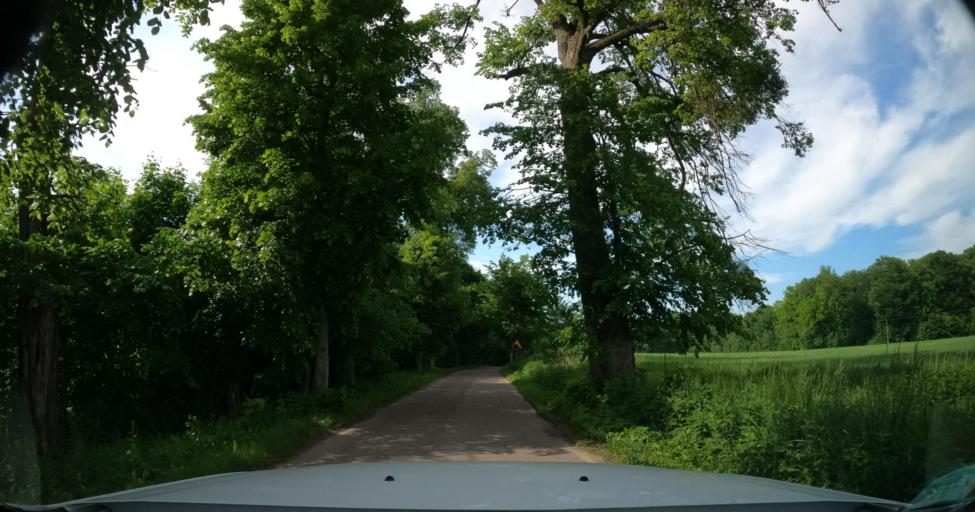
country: PL
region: Warmian-Masurian Voivodeship
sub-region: Powiat ostrodzki
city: Morag
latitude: 54.0245
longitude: 19.9123
